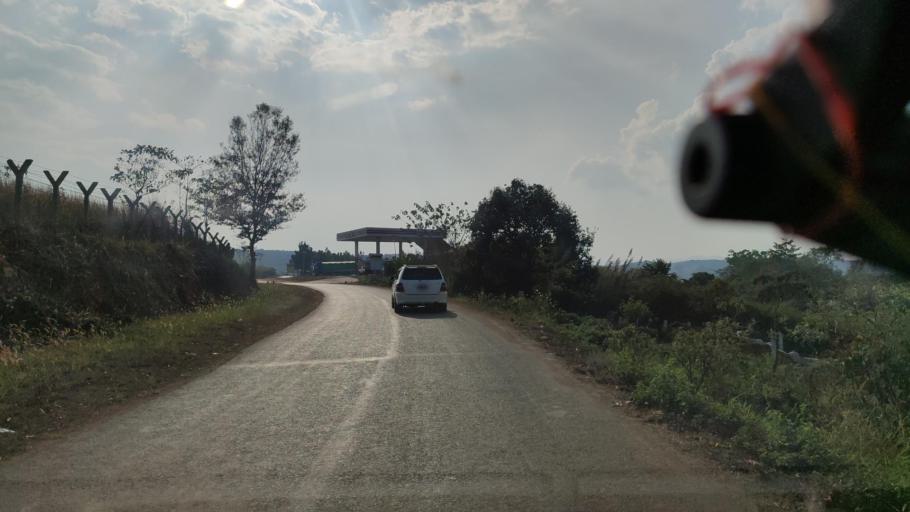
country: CN
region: Yunnan
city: Nayun
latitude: 21.8447
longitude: 99.6703
